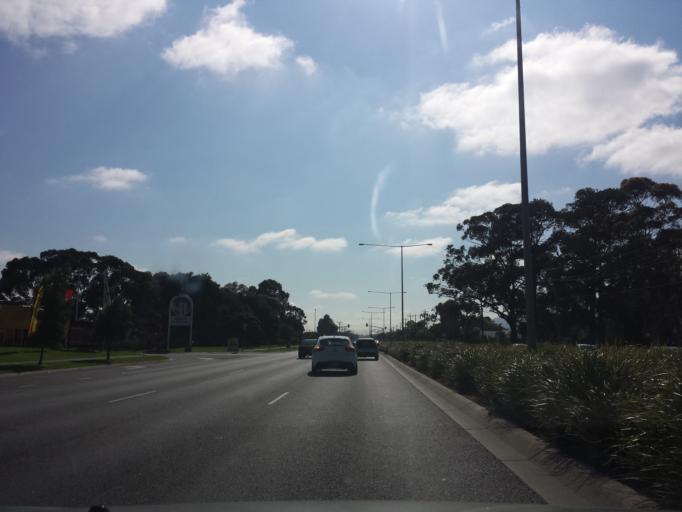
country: AU
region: Victoria
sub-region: Maroondah
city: Croydon South
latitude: -37.8311
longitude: 145.2727
